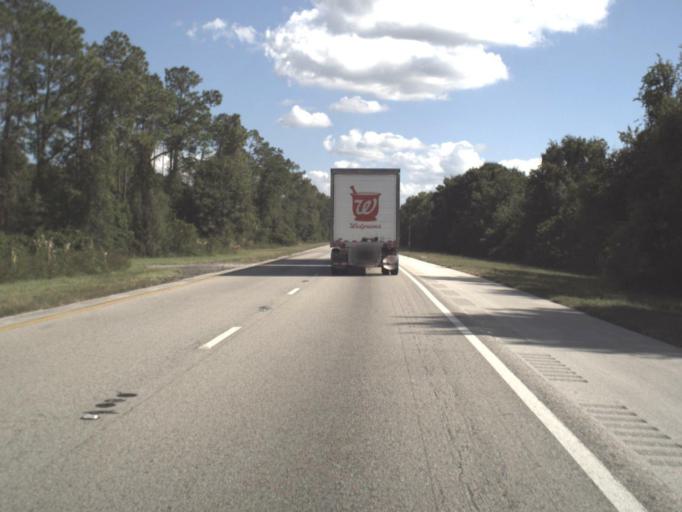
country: US
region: Florida
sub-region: Osceola County
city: Saint Cloud
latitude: 28.0550
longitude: -81.2265
